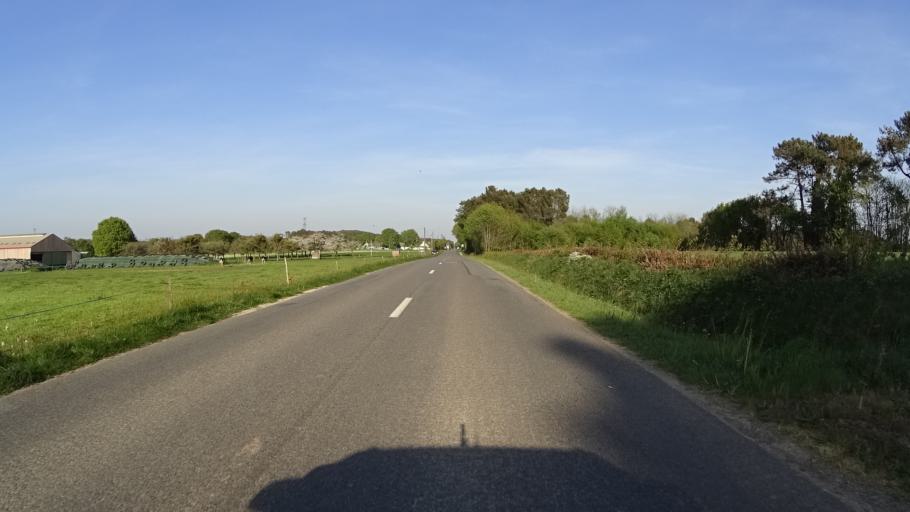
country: FR
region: Brittany
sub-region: Departement du Morbihan
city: Allaire
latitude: 47.6112
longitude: -2.1821
